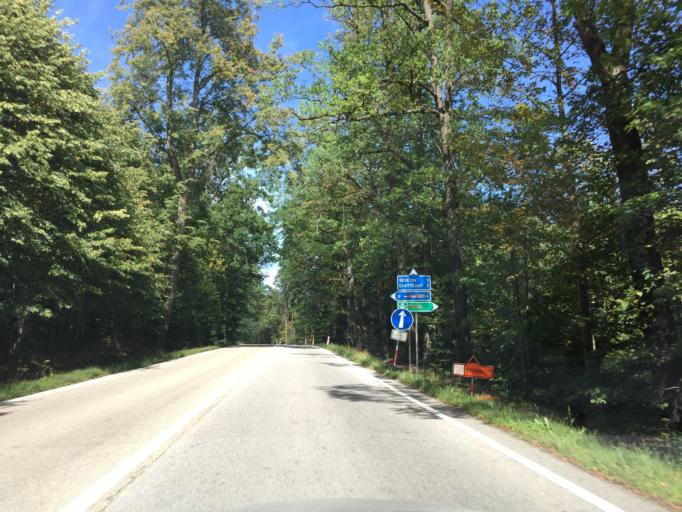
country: CZ
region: Jihocesky
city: Borek
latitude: 49.0503
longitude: 14.5109
